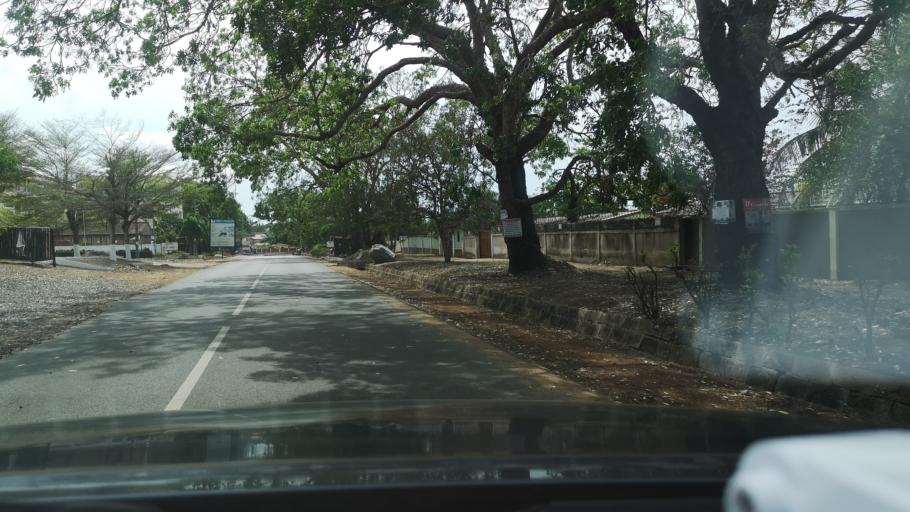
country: GH
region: Greater Accra
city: Tema
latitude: 5.6567
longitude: -0.0243
